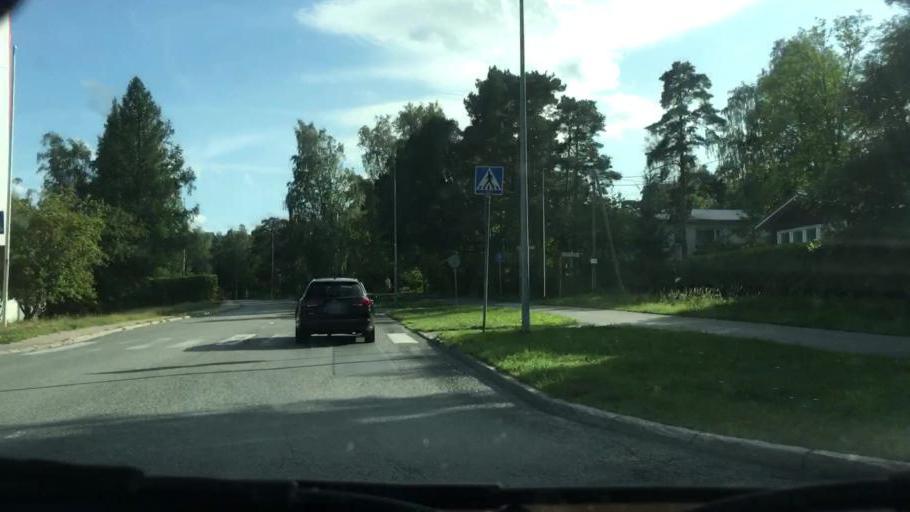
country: FI
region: Varsinais-Suomi
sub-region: Turku
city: Turku
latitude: 60.4692
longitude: 22.2350
